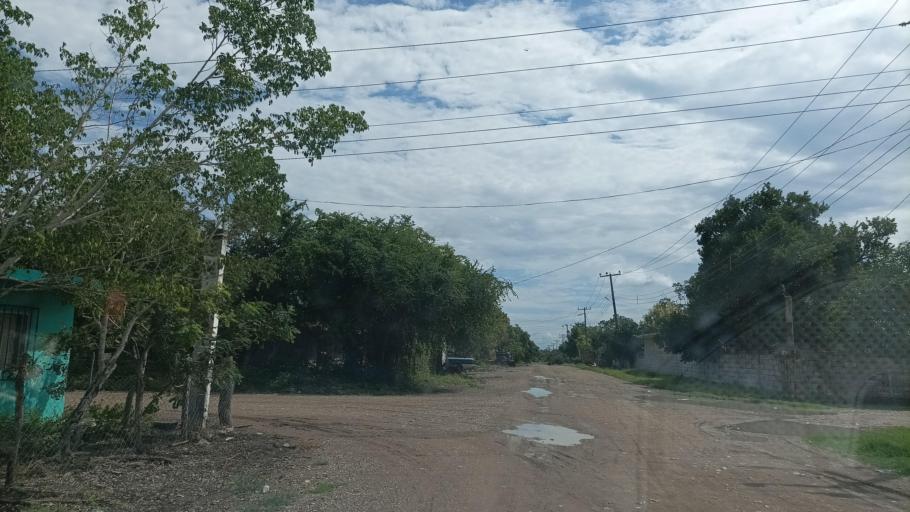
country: MX
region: Veracruz
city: Panuco
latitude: 21.9479
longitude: -98.1368
